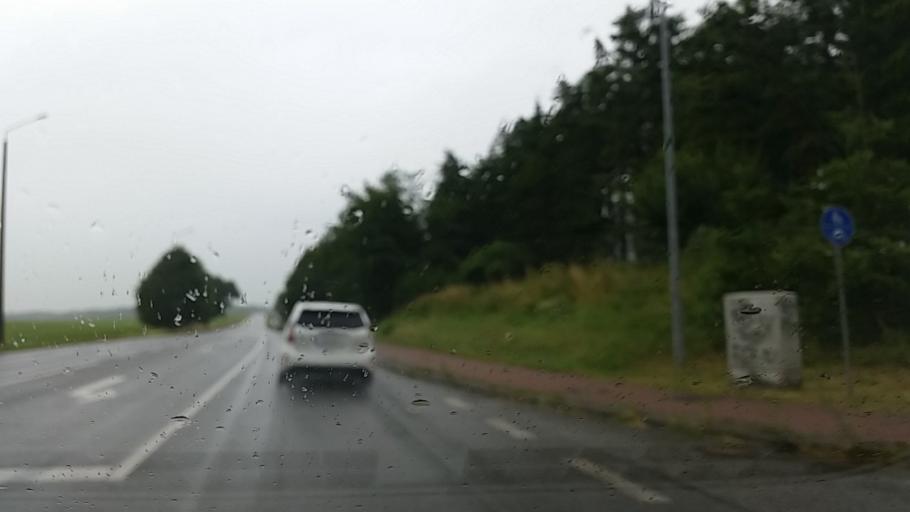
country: DE
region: Mecklenburg-Vorpommern
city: Bad Doberan
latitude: 54.0894
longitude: 11.8563
